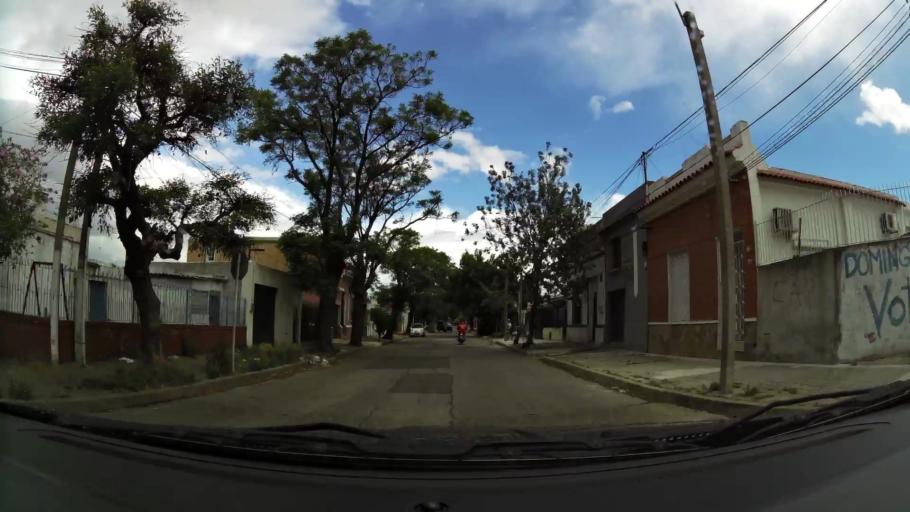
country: UY
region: Montevideo
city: Montevideo
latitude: -34.8553
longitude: -56.1678
